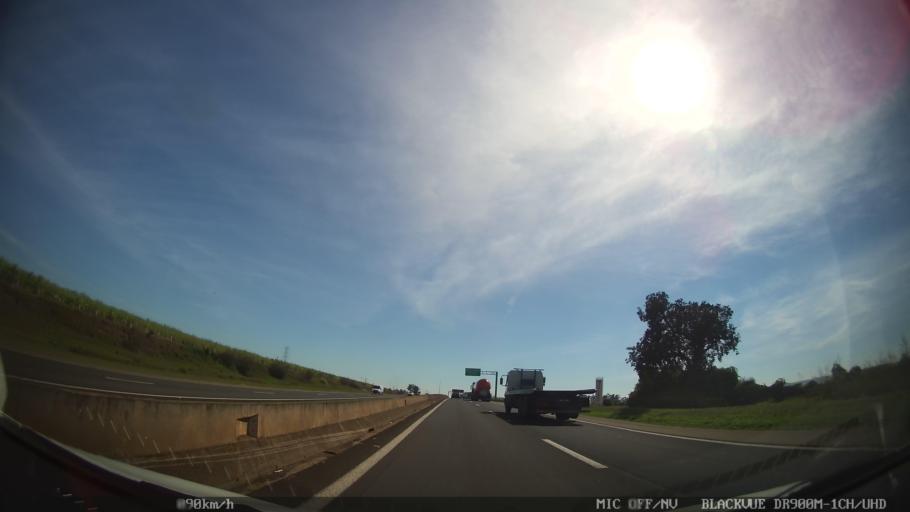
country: BR
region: Sao Paulo
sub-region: Porto Ferreira
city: Porto Ferreira
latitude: -21.8880
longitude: -47.4833
